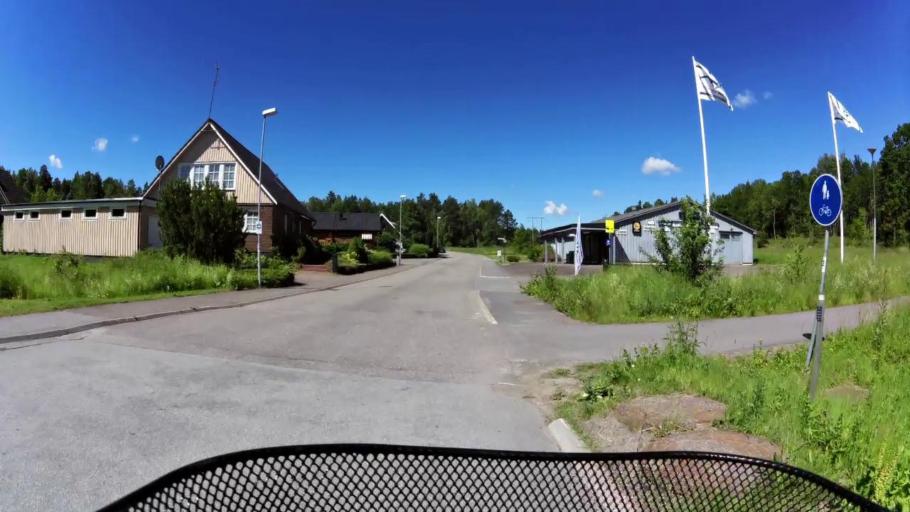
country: SE
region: OEstergoetland
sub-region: Linkopings Kommun
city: Sturefors
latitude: 58.3893
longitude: 15.6988
